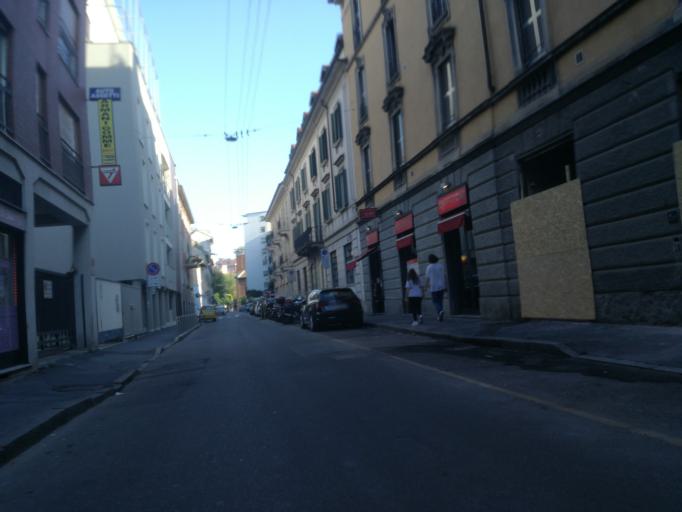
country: IT
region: Lombardy
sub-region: Citta metropolitana di Milano
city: Milano
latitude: 45.4506
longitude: 9.2010
